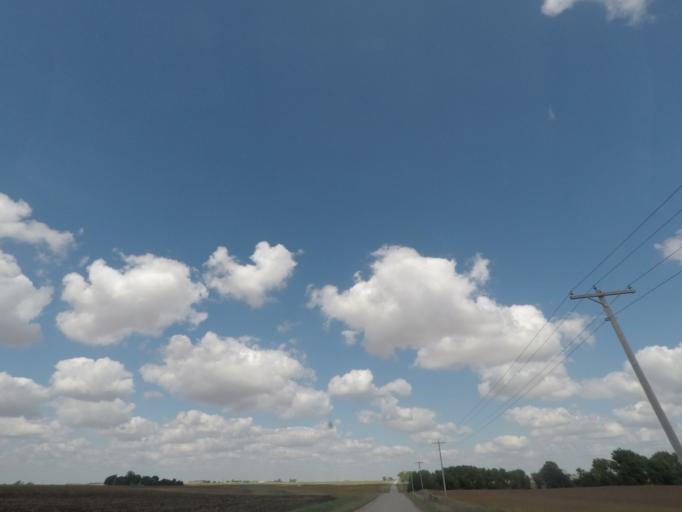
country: US
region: Iowa
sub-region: Story County
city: Nevada
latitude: 42.0720
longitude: -93.3864
